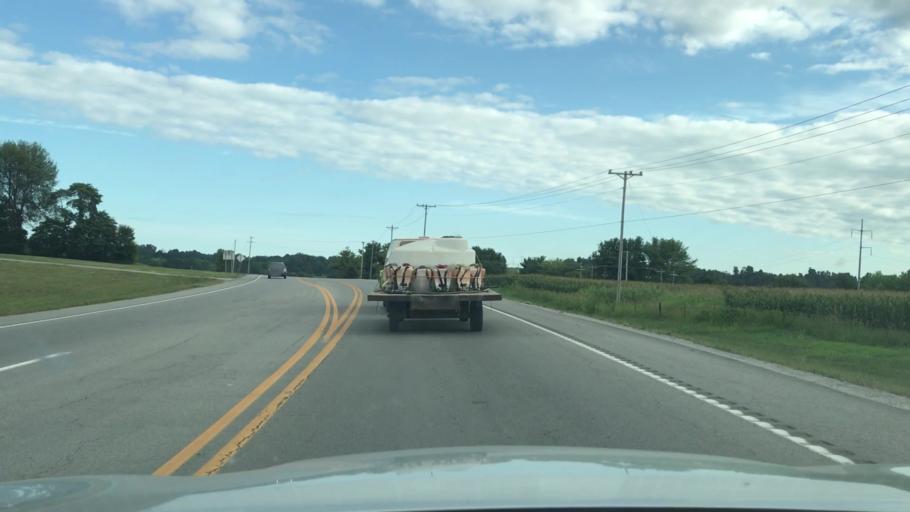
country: US
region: Kentucky
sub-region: Todd County
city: Elkton
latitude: 36.8251
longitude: -87.1511
